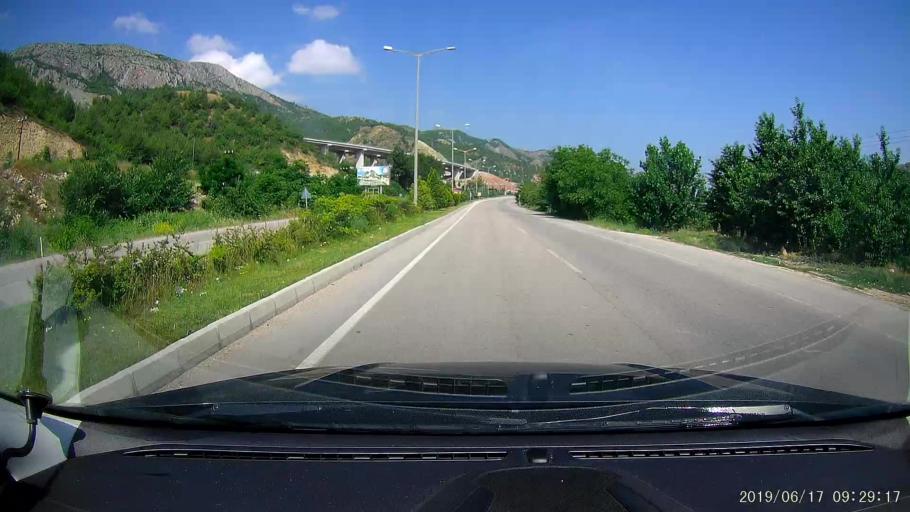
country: TR
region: Amasya
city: Amasya
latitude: 40.6955
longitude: 35.8139
